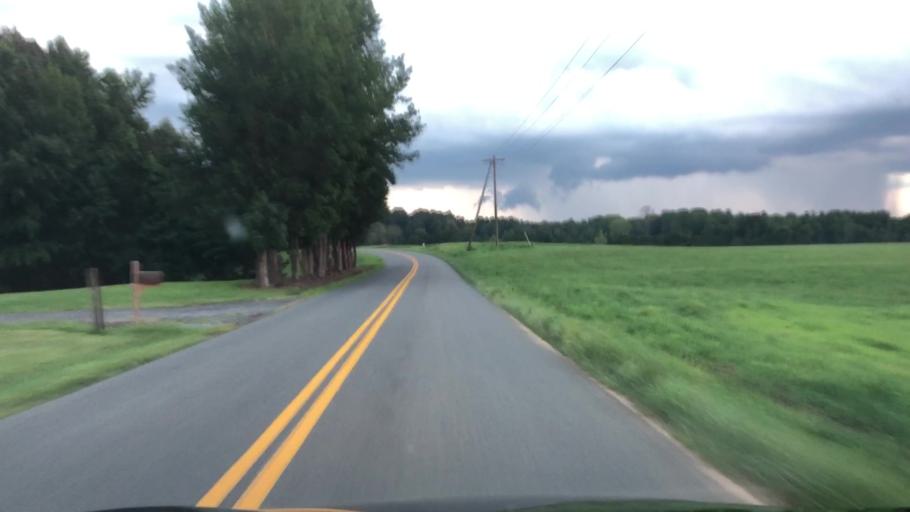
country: US
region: Virginia
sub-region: Stafford County
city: Falmouth
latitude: 38.4443
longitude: -77.5910
